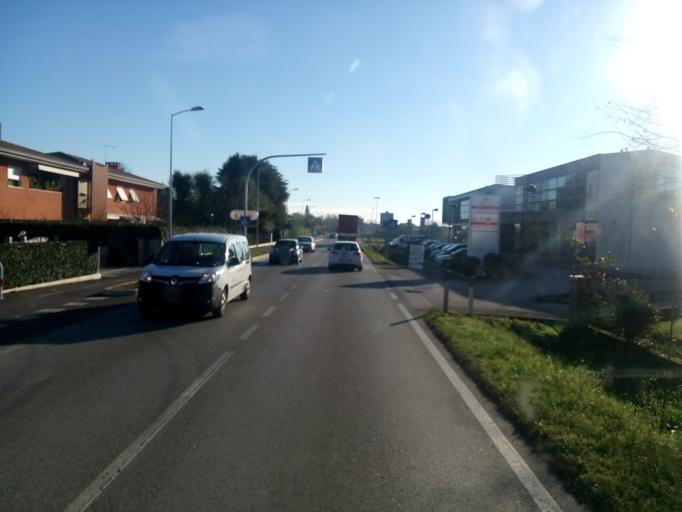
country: IT
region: Veneto
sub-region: Provincia di Treviso
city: Castello di Godego
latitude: 45.6951
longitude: 11.8699
